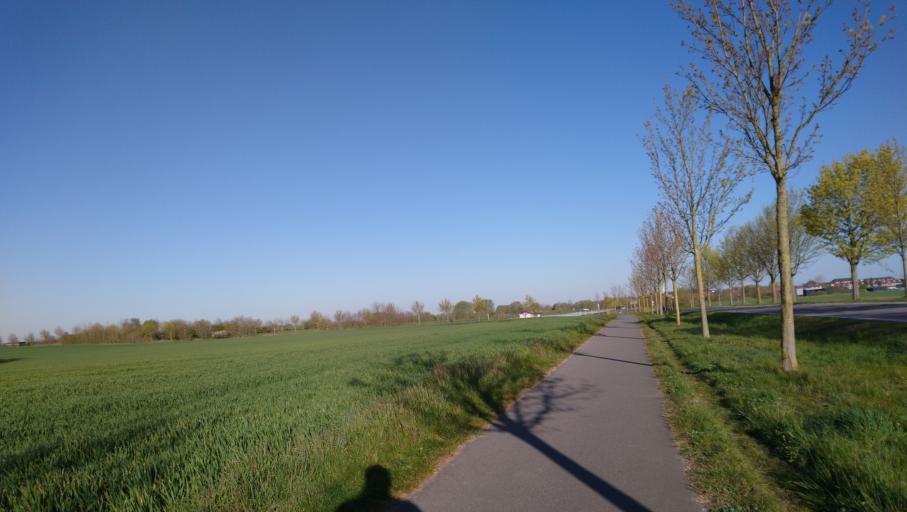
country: DE
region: Mecklenburg-Vorpommern
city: Papendorf
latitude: 54.0542
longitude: 12.1248
